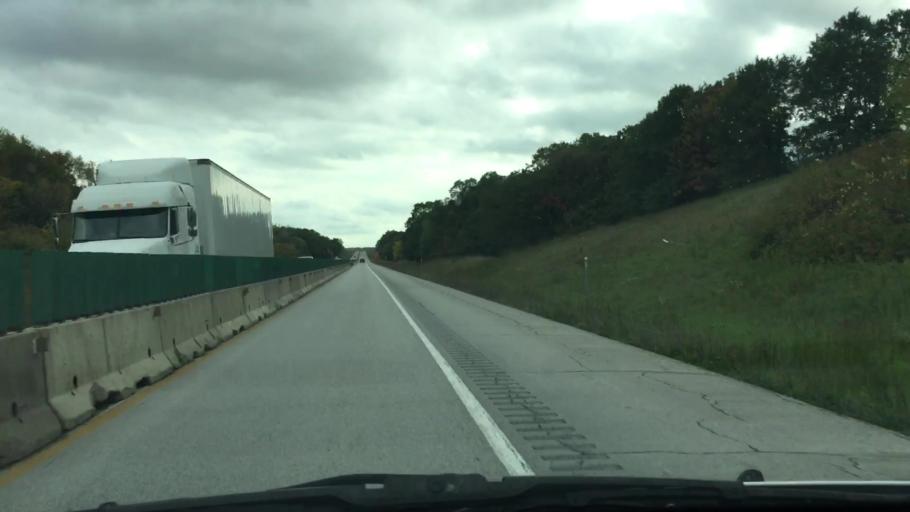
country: US
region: Iowa
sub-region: Decatur County
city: Leon
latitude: 40.7007
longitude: -93.8460
